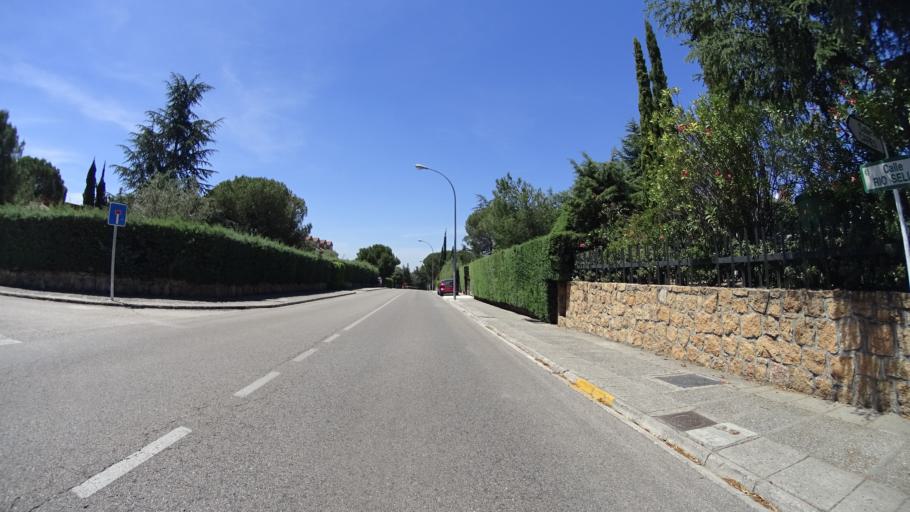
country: ES
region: Madrid
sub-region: Provincia de Madrid
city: Hoyo de Manzanares
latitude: 40.6100
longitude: -3.9366
